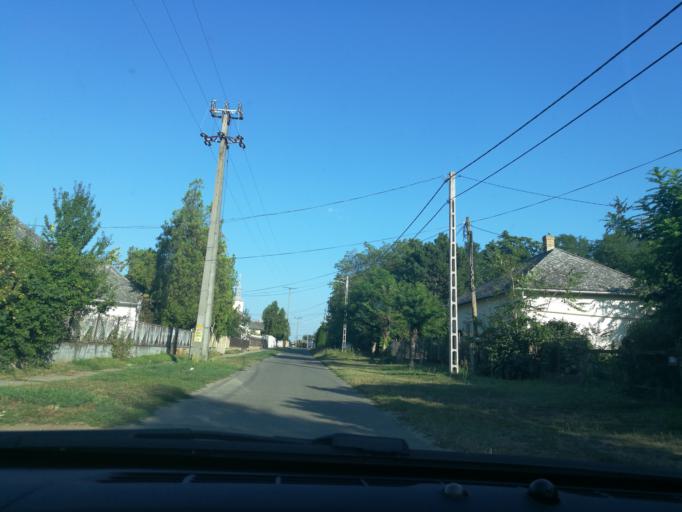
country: HU
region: Szabolcs-Szatmar-Bereg
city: Tiszabercel
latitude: 48.1639
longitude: 21.5930
